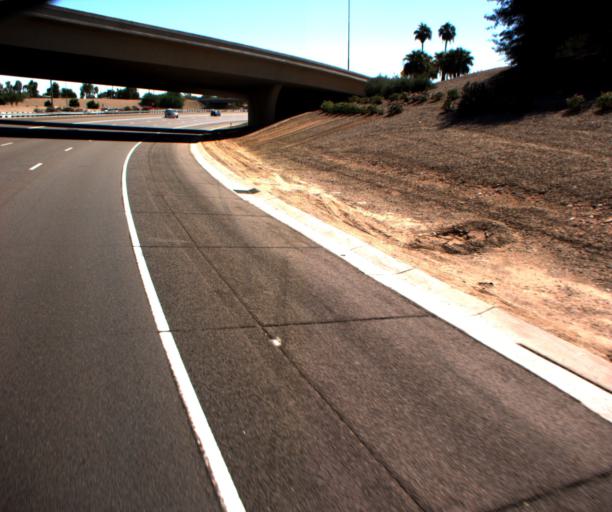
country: US
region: Arizona
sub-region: Maricopa County
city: Phoenix
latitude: 33.4611
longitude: -112.0389
